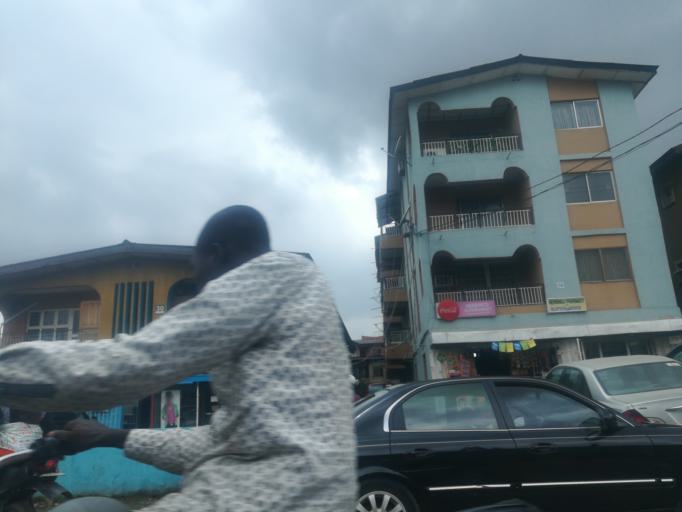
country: NG
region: Lagos
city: Ojota
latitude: 6.5972
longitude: 3.3908
